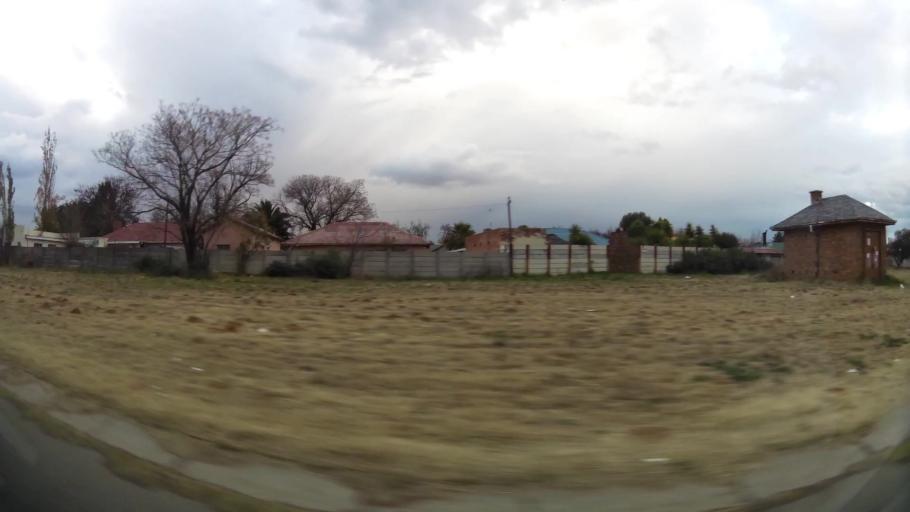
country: ZA
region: Orange Free State
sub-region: Lejweleputswa District Municipality
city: Welkom
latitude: -27.9666
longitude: 26.7413
